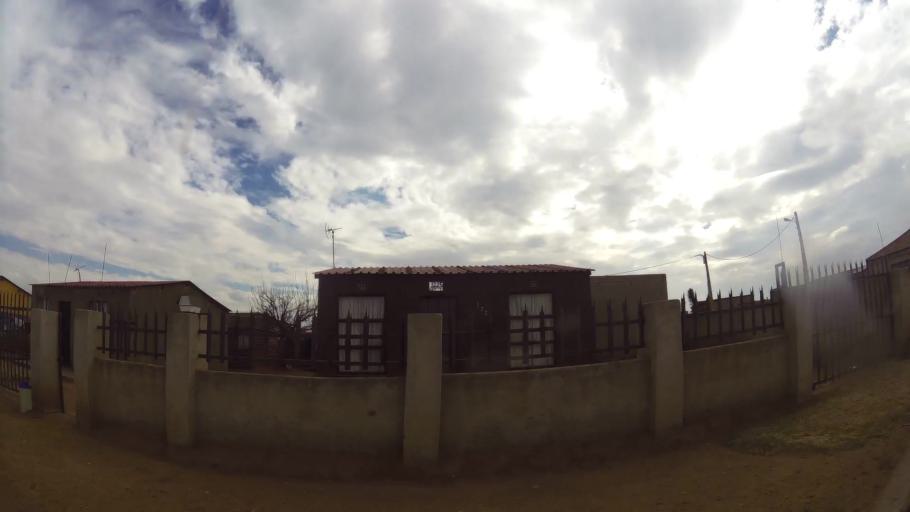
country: ZA
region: Gauteng
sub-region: Ekurhuleni Metropolitan Municipality
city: Germiston
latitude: -26.4038
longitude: 28.1419
